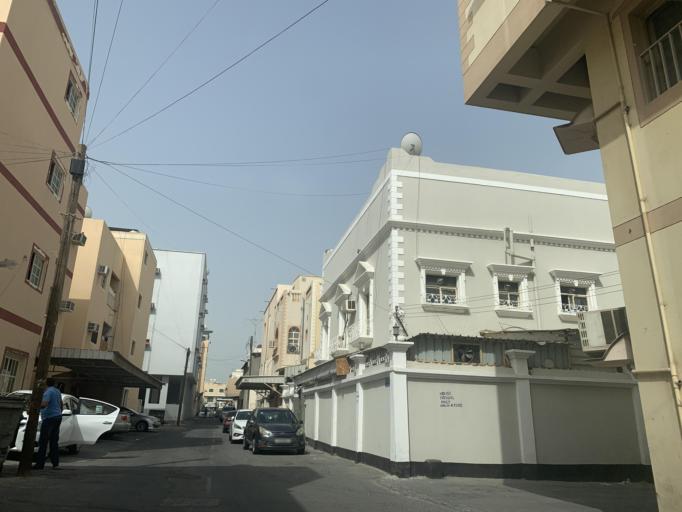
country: BH
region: Northern
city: Ar Rifa'
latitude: 26.1276
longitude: 50.5690
